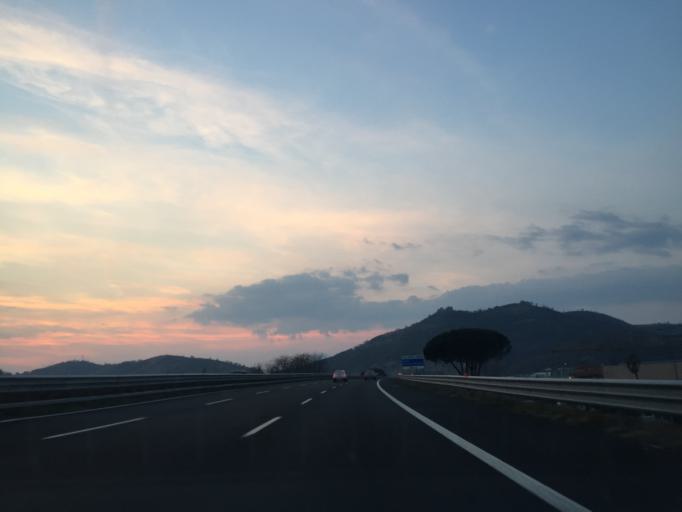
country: IT
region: Campania
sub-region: Provincia di Salerno
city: Casali-San Potito
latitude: 40.7677
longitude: 14.6768
